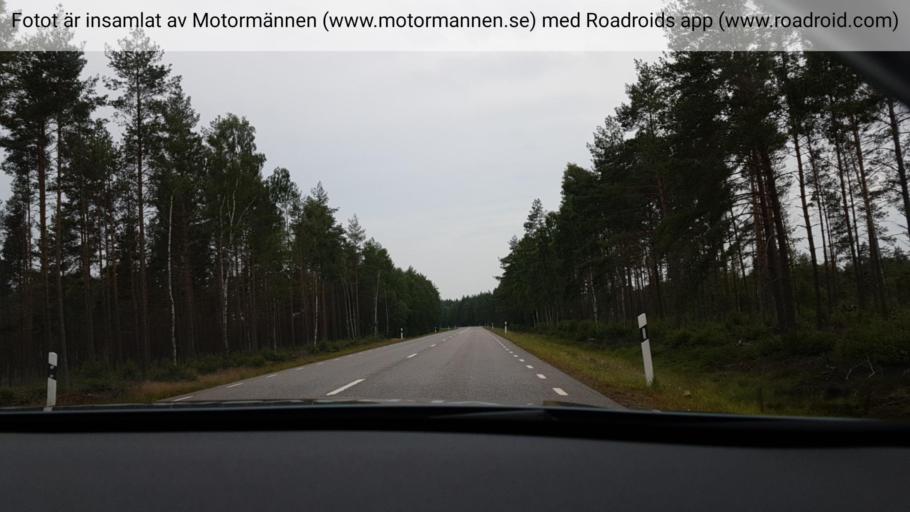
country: SE
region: Joenkoeping
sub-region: Varnamo Kommun
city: Bor
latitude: 57.2790
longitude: 14.2510
